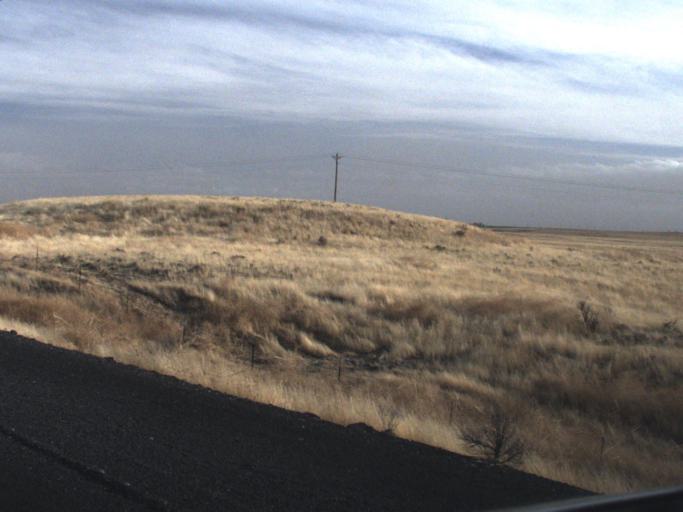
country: US
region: Washington
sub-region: Grant County
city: Warden
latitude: 47.3196
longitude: -118.8579
